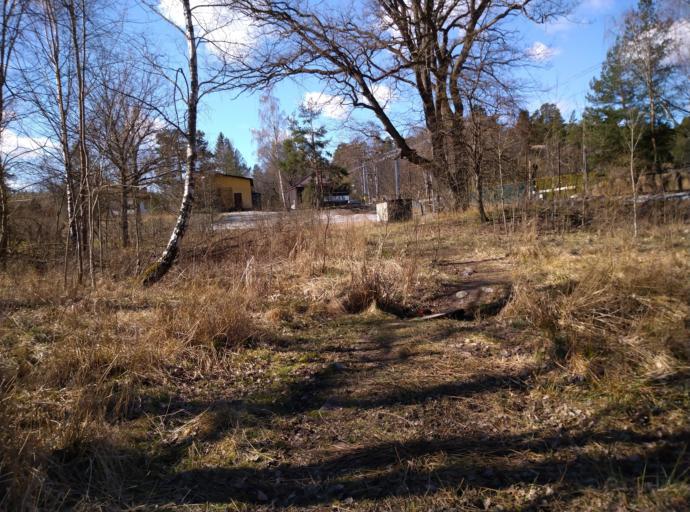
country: SE
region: Stockholm
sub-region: Nacka Kommun
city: Fisksatra
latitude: 59.2955
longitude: 18.2370
